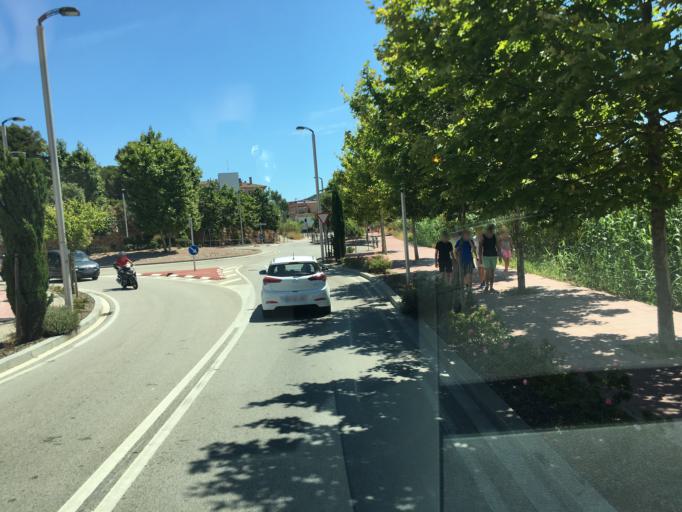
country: ES
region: Catalonia
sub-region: Provincia de Girona
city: Lloret de Mar
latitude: 41.7040
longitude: 2.8560
